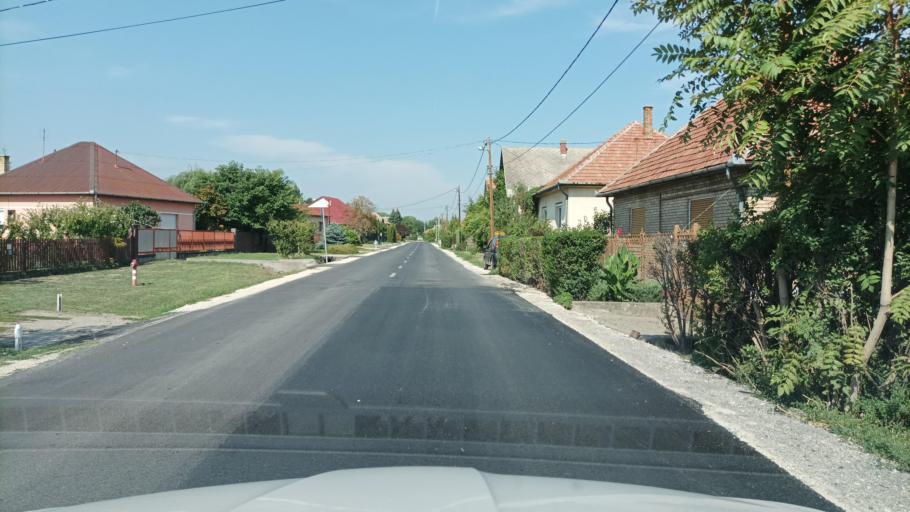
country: HU
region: Pest
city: Tura
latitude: 47.6017
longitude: 19.5945
